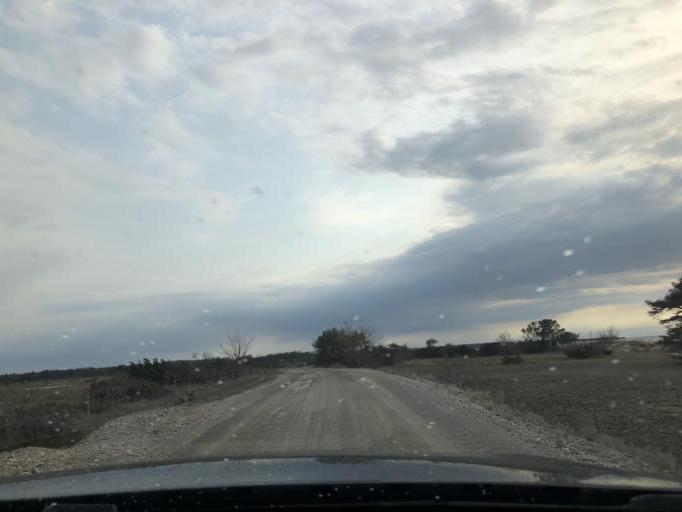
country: SE
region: Kalmar
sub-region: Borgholms Kommun
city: Borgholm
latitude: 57.2209
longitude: 16.9511
